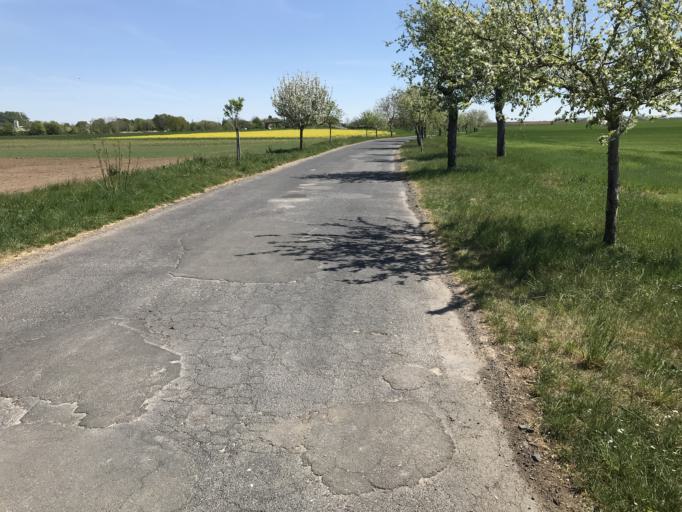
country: DE
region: Bavaria
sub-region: Regierungsbezirk Unterfranken
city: Iphofen
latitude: 49.6877
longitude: 10.2724
